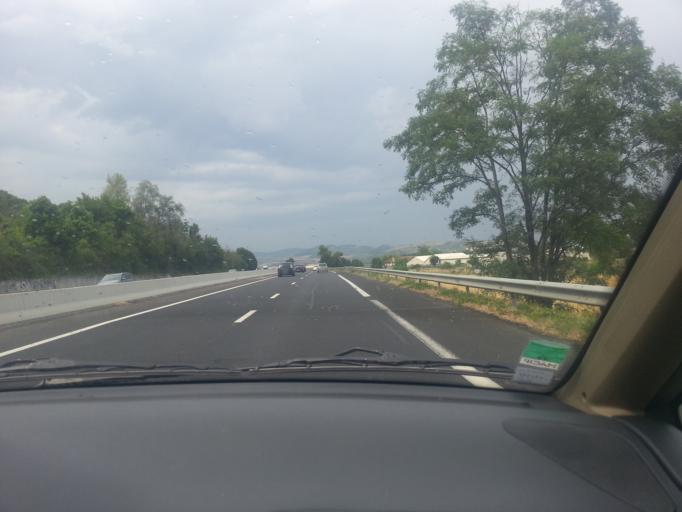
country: FR
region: Auvergne
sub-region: Departement du Puy-de-Dome
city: Le Breuil-sur-Couze
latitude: 45.5078
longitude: 3.2626
